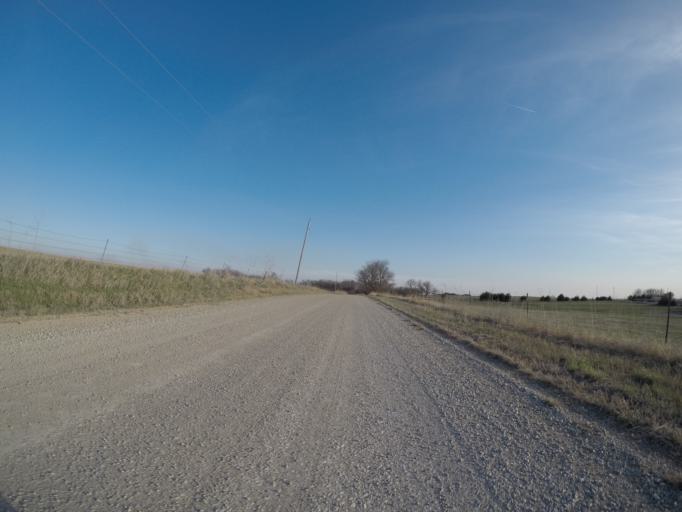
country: US
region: Kansas
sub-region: Riley County
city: Manhattan
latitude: 39.2451
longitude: -96.6913
